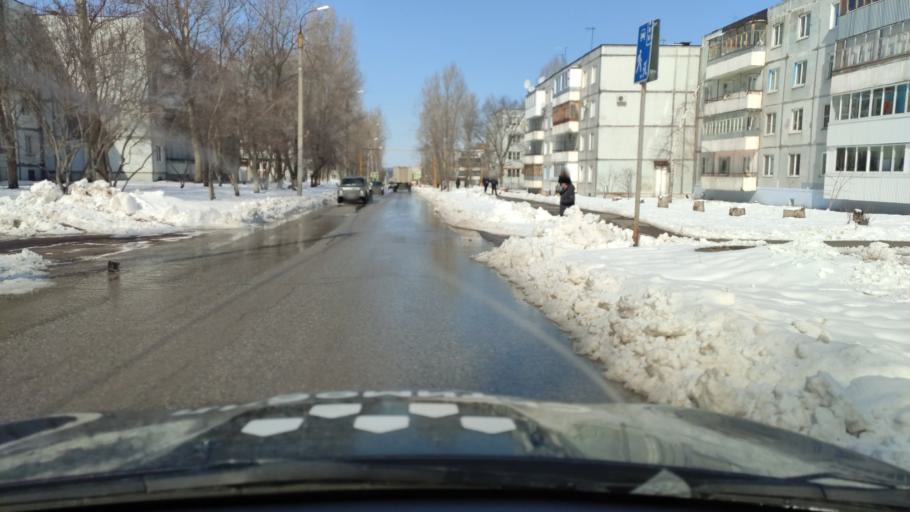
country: RU
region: Samara
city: Povolzhskiy
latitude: 53.5860
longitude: 49.7663
